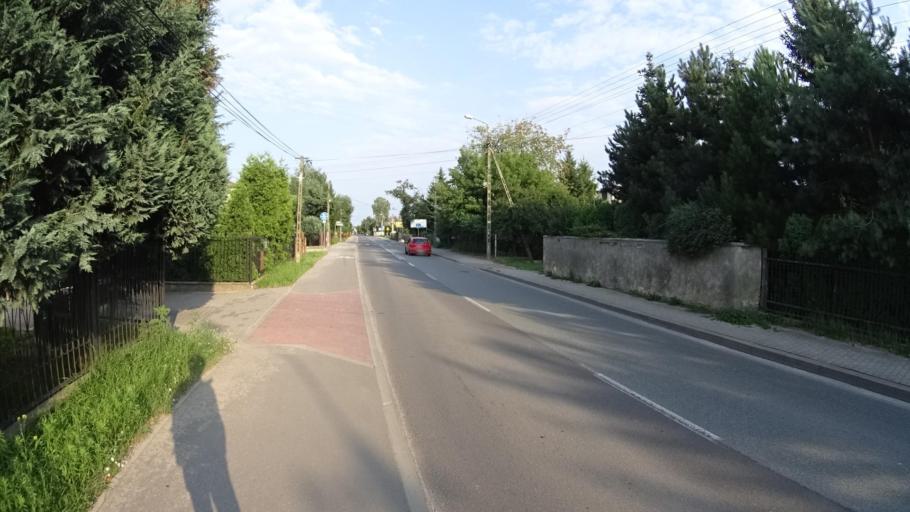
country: PL
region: Masovian Voivodeship
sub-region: Powiat pruszkowski
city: Rybie
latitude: 52.1476
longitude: 20.9437
